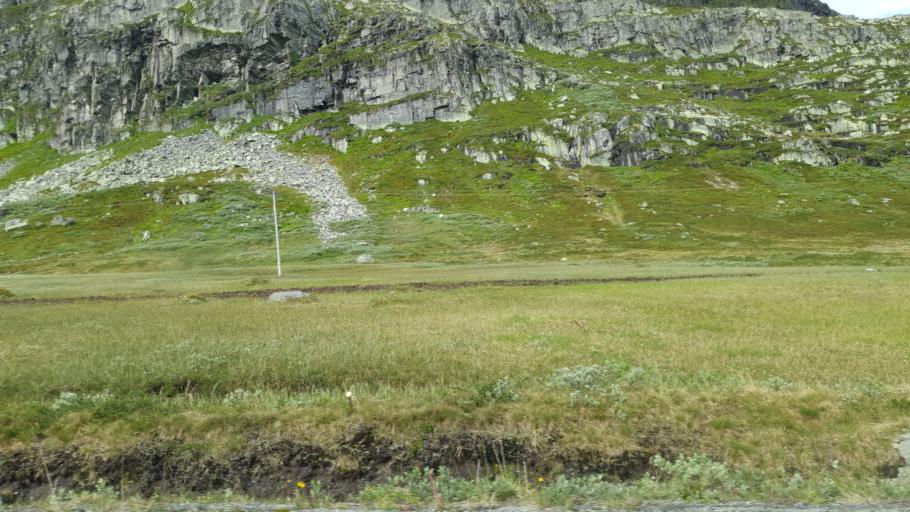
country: NO
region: Oppland
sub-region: Vestre Slidre
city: Slidre
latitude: 61.3059
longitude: 8.8077
